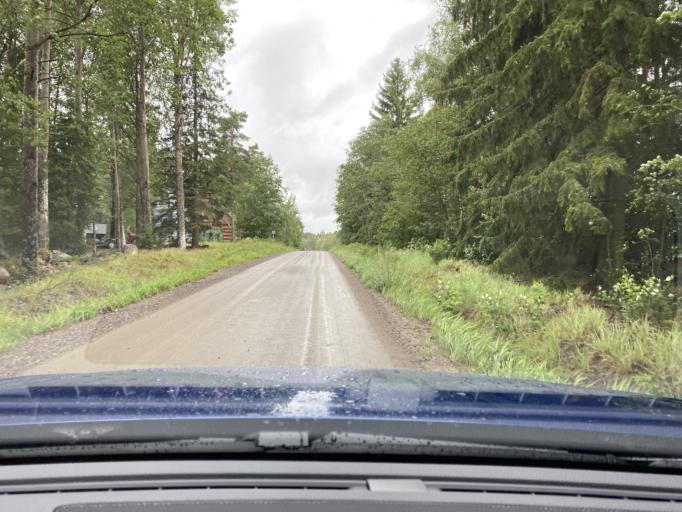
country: FI
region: Pirkanmaa
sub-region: Lounais-Pirkanmaa
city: Punkalaidun
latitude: 61.1493
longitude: 23.2352
